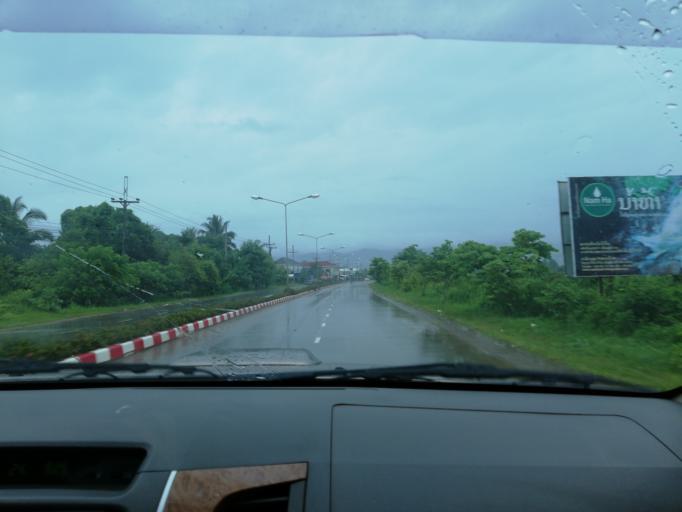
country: LA
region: Loungnamtha
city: Louang Namtha
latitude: 20.9559
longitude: 101.4039
